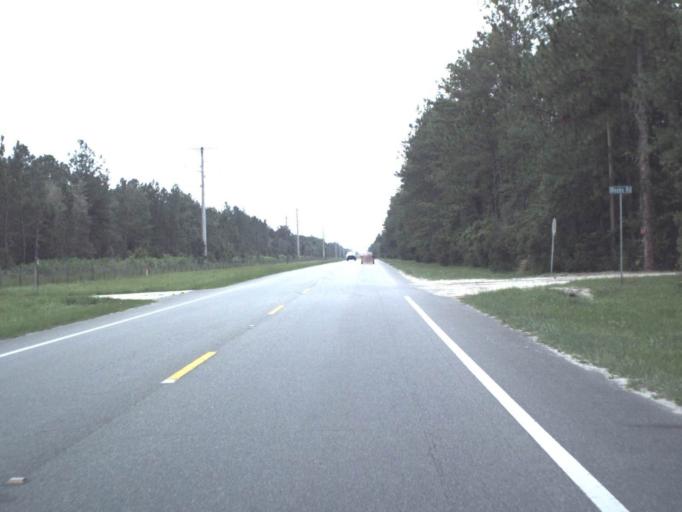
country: US
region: Florida
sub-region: Clay County
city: Middleburg
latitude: 29.9556
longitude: -81.8977
